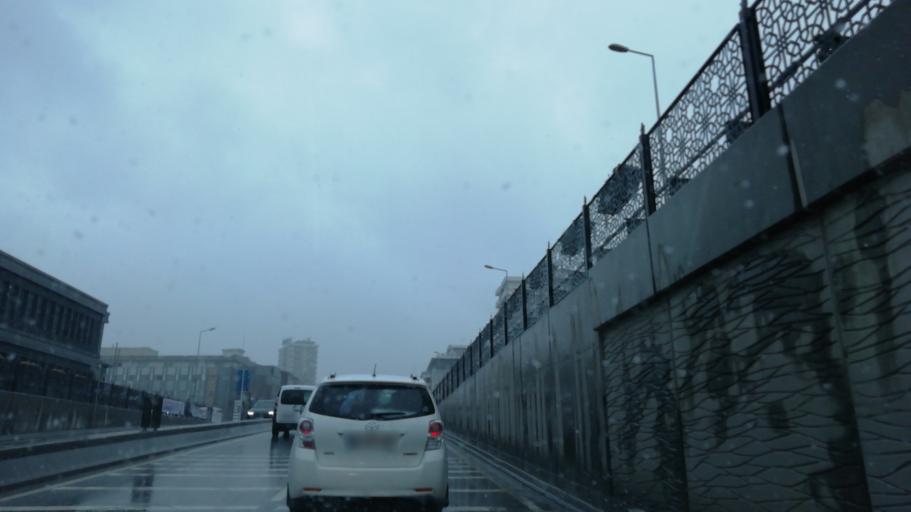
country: TR
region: Istanbul
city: Esenyurt
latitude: 41.0223
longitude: 28.6870
